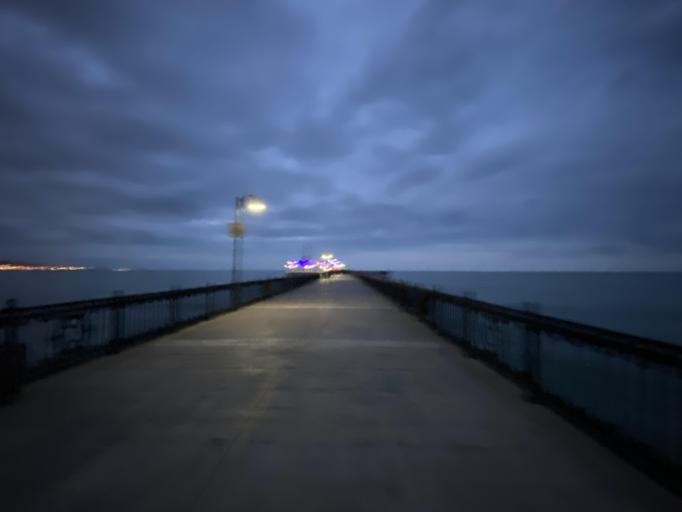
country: TR
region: Samsun
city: Samsun
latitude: 41.3447
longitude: 36.2619
